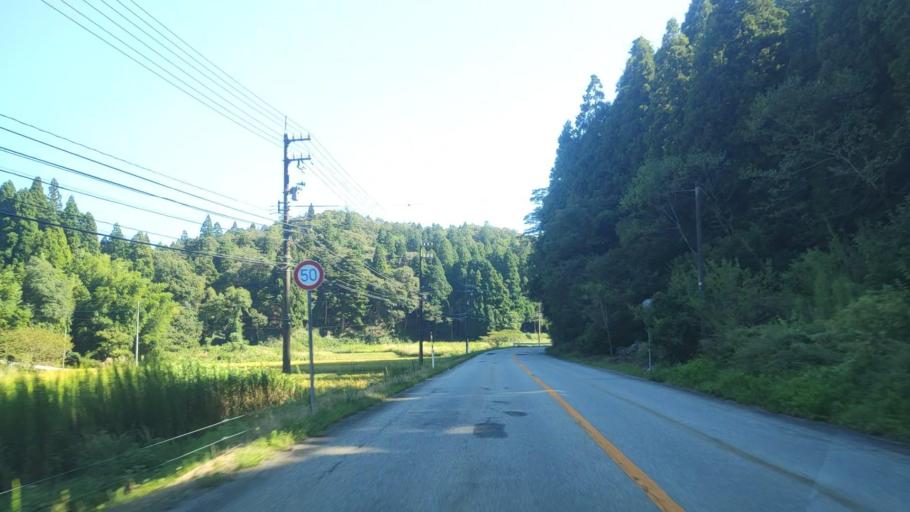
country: JP
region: Ishikawa
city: Nanao
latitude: 37.3318
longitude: 137.2082
